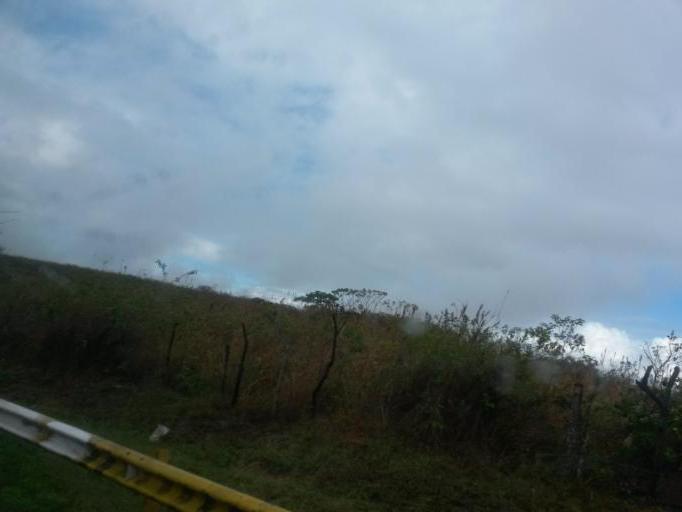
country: CO
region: Cauca
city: El Bordo
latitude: 2.1464
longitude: -76.9286
